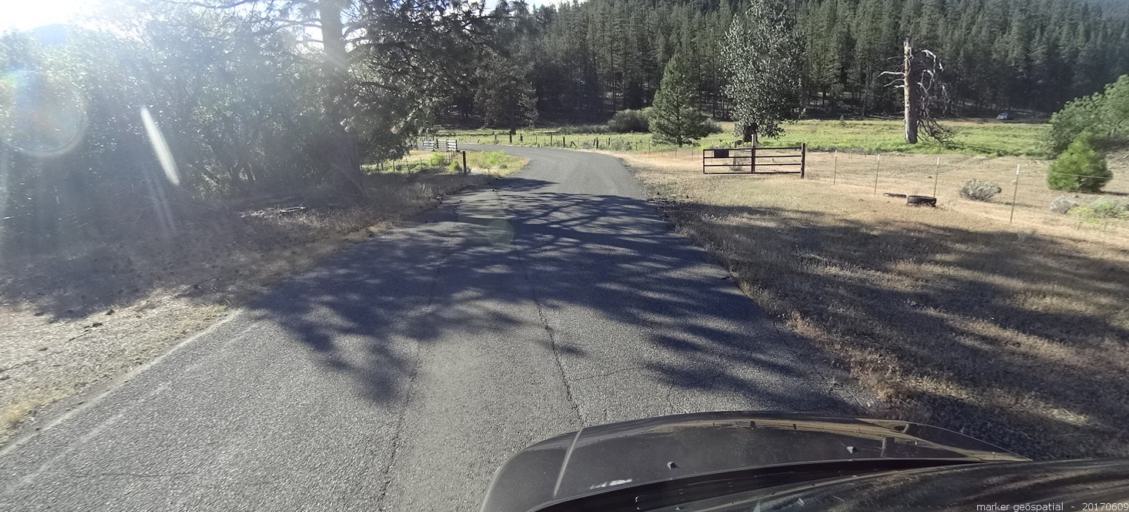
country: US
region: California
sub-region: Siskiyou County
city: Weed
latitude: 41.3255
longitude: -122.7215
